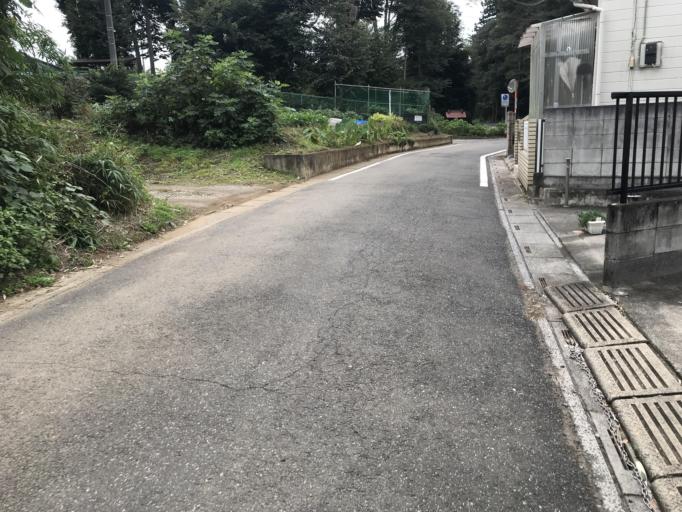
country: JP
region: Saitama
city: Shiraoka
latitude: 36.0047
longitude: 139.6568
